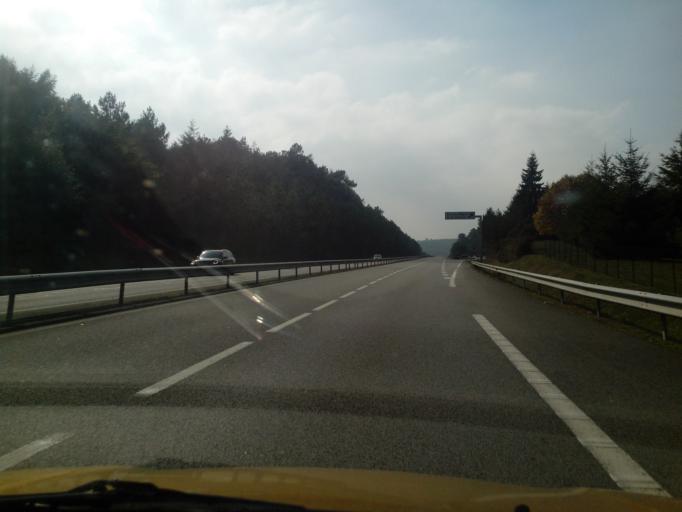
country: FR
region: Brittany
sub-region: Departement du Morbihan
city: Malestroit
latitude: 47.8025
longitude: -2.4451
